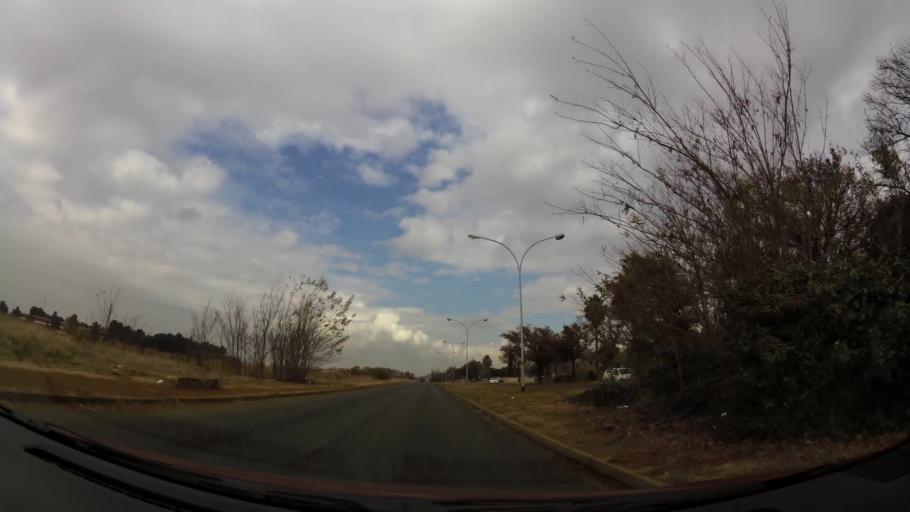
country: ZA
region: Gauteng
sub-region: Sedibeng District Municipality
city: Vanderbijlpark
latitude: -26.7195
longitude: 27.8631
